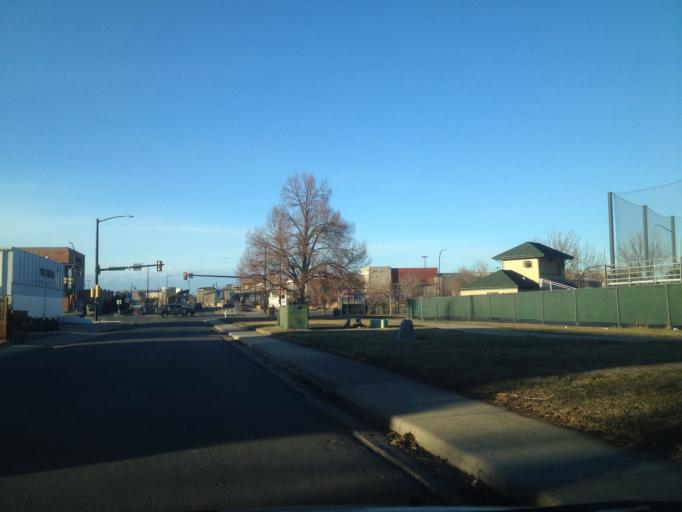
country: US
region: Colorado
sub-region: Boulder County
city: Boulder
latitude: 40.0137
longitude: -105.2561
